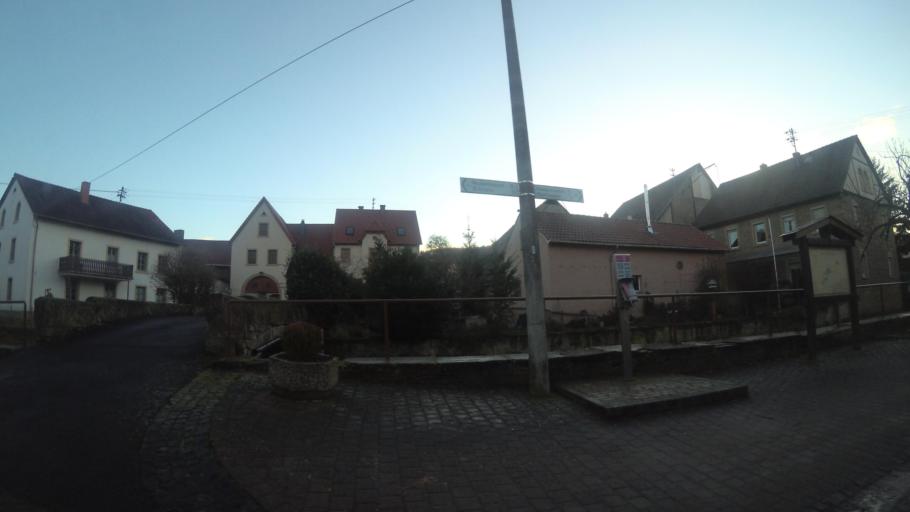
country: DE
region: Rheinland-Pfalz
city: Niedermoschel
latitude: 49.7322
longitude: 7.7946
